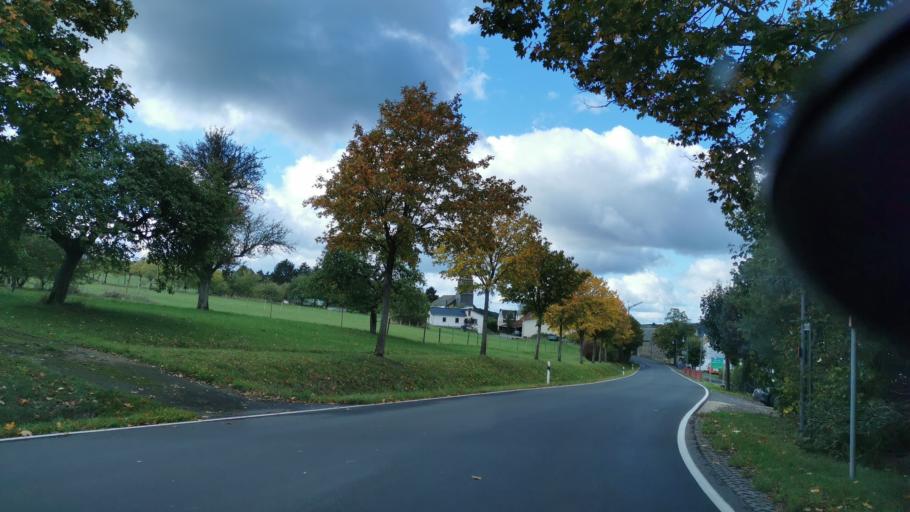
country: DE
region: Rheinland-Pfalz
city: Walsdorf
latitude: 50.2800
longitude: 6.7180
